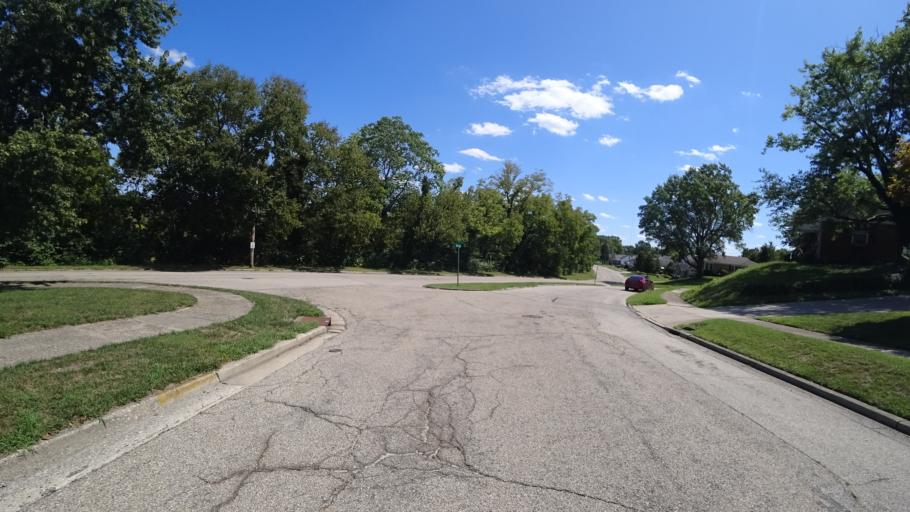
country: US
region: Ohio
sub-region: Butler County
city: New Miami
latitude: 39.4101
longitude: -84.5354
